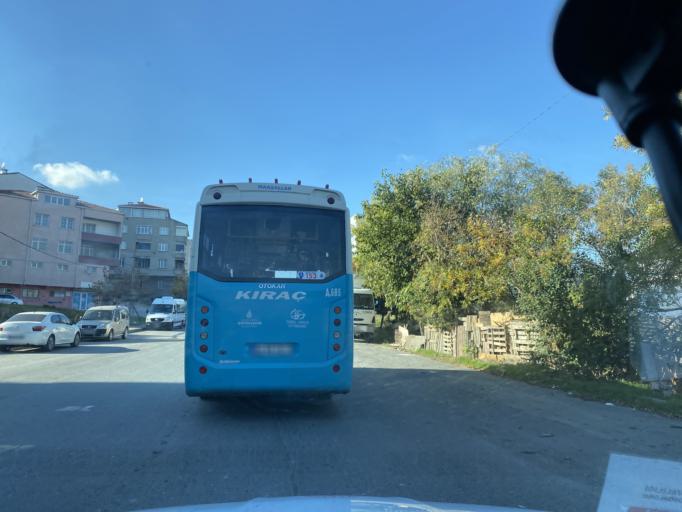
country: TR
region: Istanbul
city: Esenyurt
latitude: 41.0464
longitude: 28.6495
